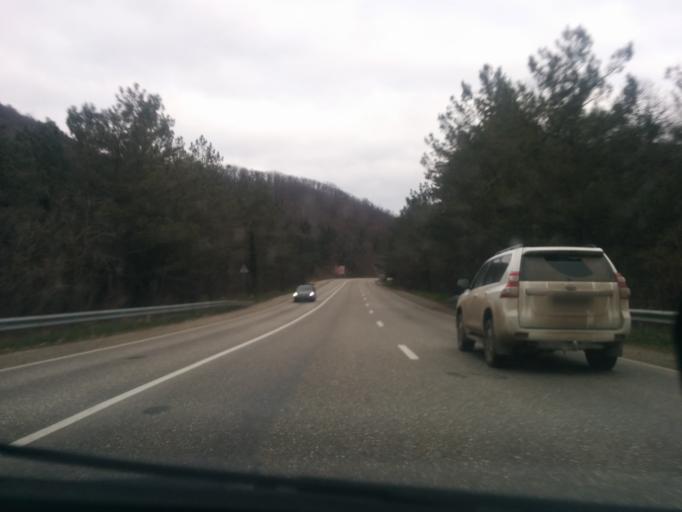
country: RU
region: Krasnodarskiy
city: Ol'ginka
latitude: 44.1824
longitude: 38.9296
